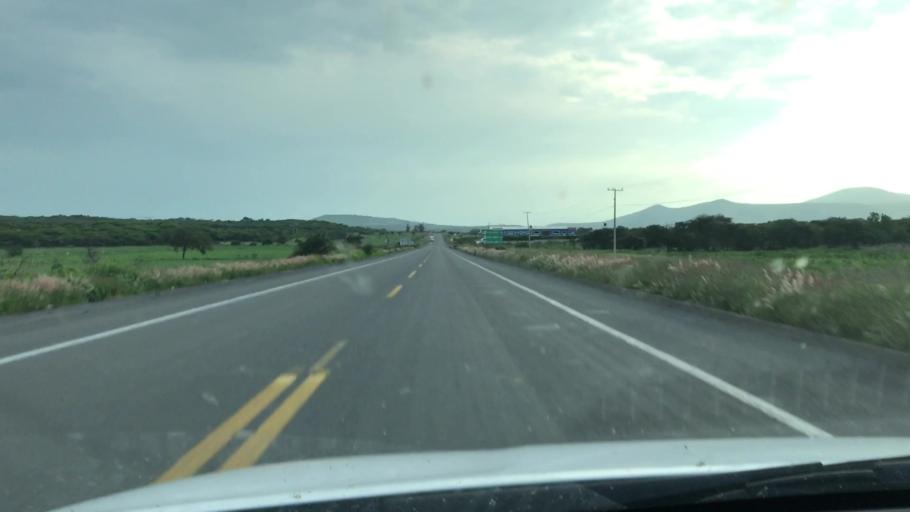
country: MX
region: Jalisco
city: Degollado
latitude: 20.3650
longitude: -102.1362
